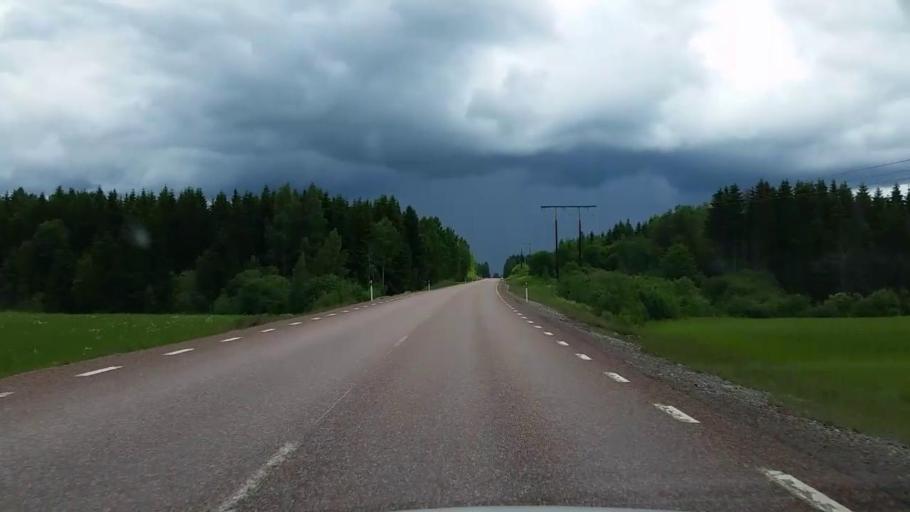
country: SE
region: Gaevleborg
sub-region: Hofors Kommun
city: Hofors
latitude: 60.5404
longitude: 16.4630
